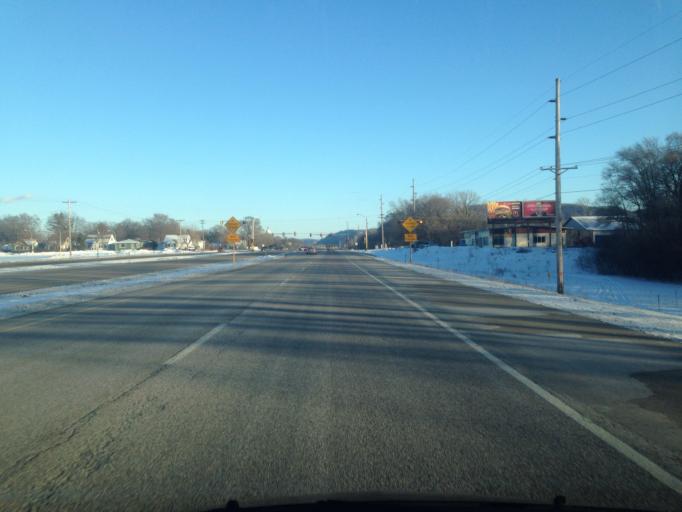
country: US
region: Minnesota
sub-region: Winona County
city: Goodview
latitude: 44.0612
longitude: -91.7054
